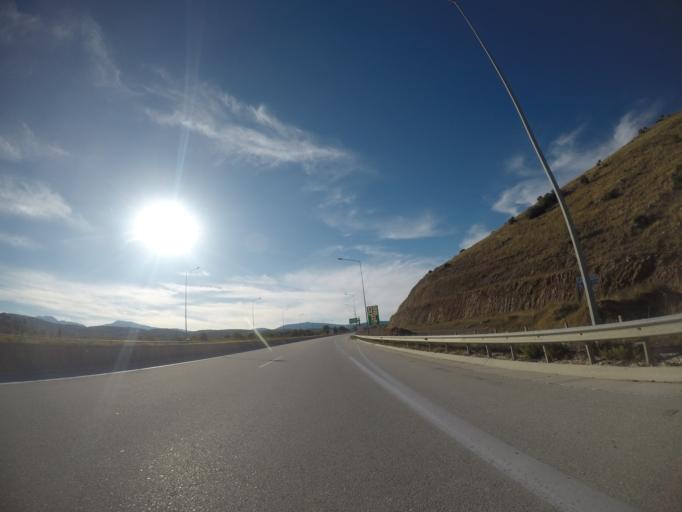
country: GR
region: Epirus
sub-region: Nomos Ioanninon
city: Koutselio
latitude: 39.5977
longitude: 20.9180
